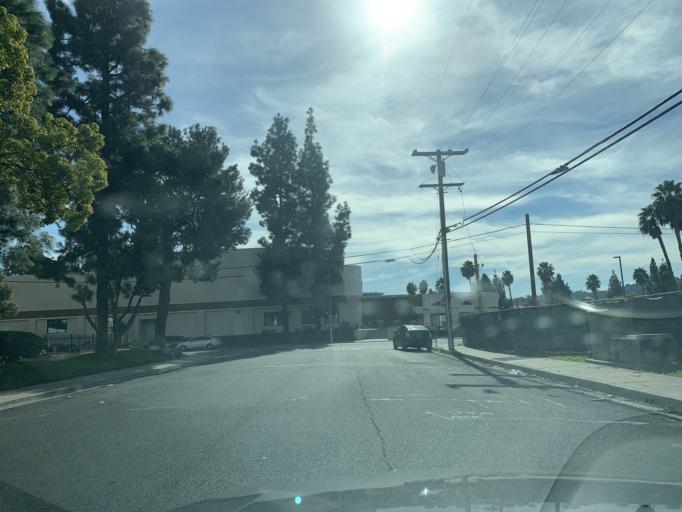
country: US
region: California
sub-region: San Diego County
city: El Cajon
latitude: 32.7996
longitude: -116.9604
